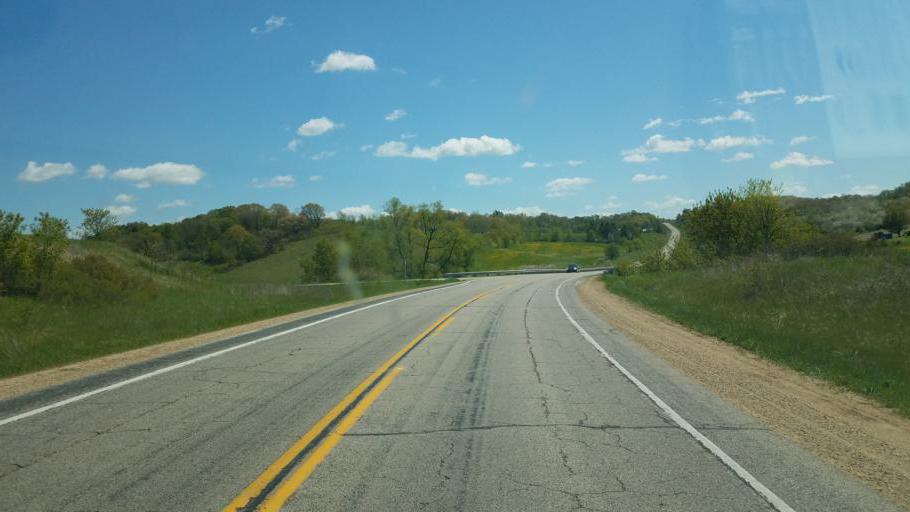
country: US
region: Wisconsin
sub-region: Vernon County
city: Hillsboro
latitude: 43.6108
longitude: -90.3532
